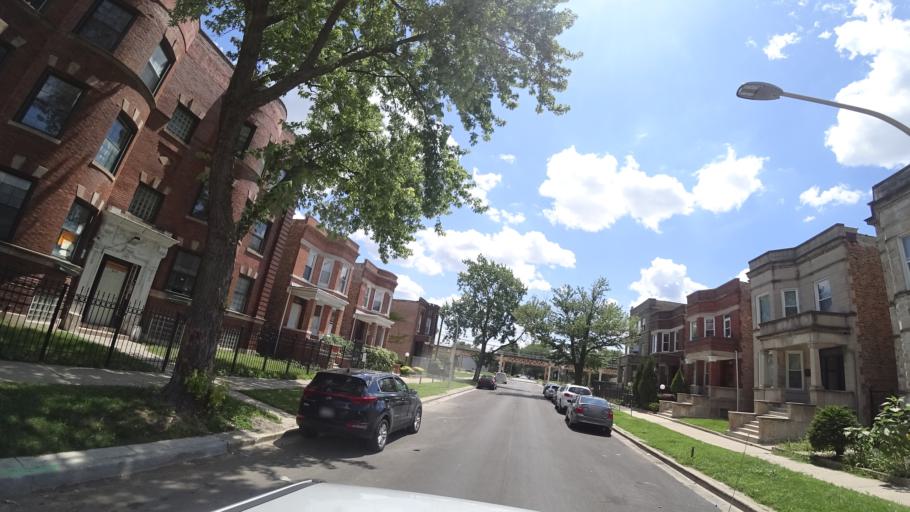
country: US
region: Illinois
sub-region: Cook County
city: Chicago
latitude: 41.7813
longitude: -87.6084
